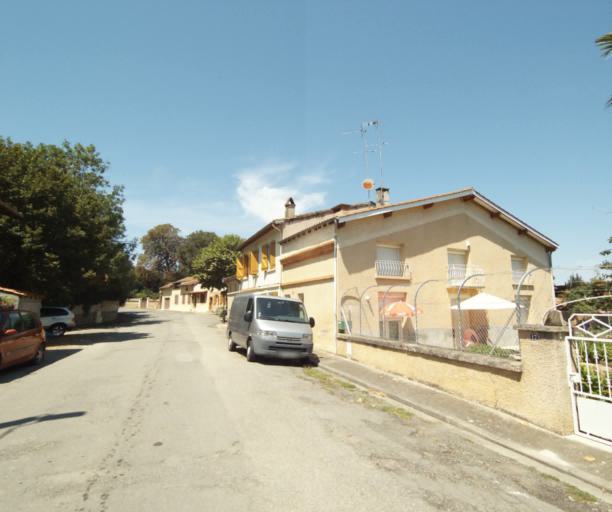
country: FR
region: Midi-Pyrenees
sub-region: Departement de l'Ariege
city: Lezat-sur-Leze
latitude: 43.2746
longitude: 1.3519
